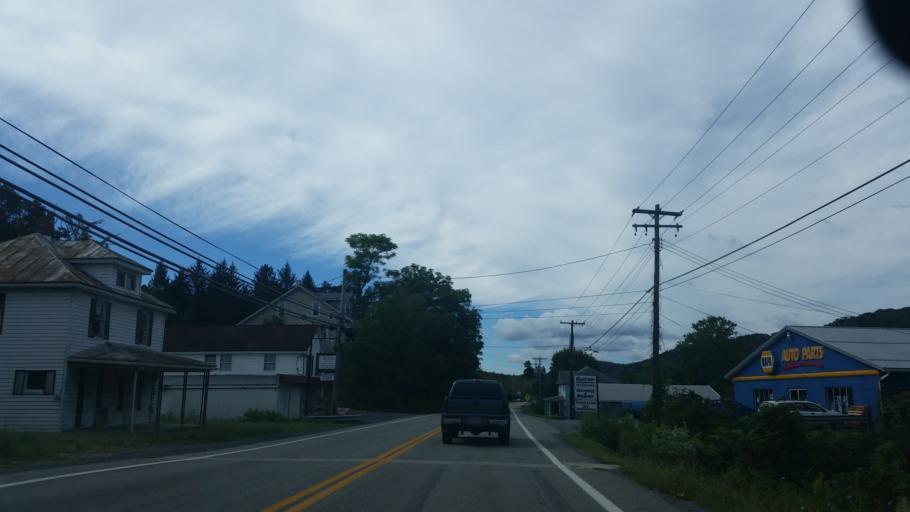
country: US
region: West Virginia
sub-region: Morgan County
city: Berkeley Springs
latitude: 39.6163
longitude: -78.2315
